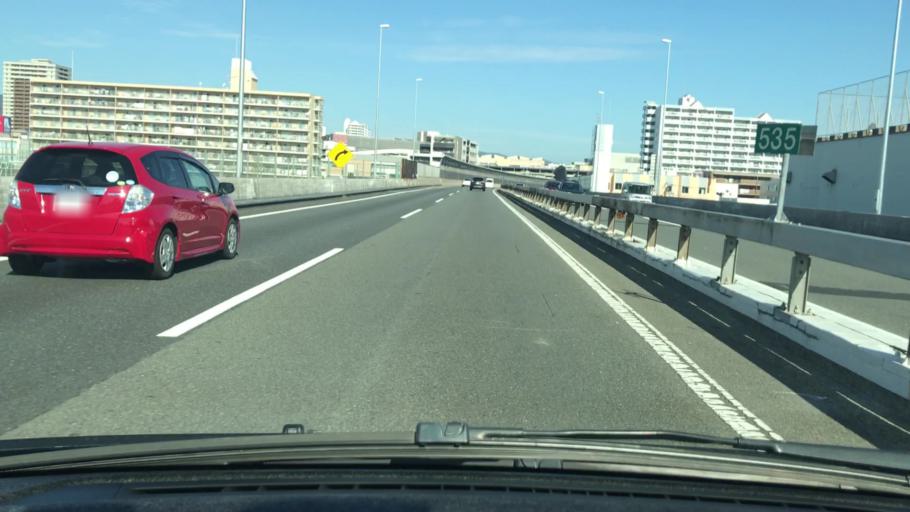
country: JP
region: Hyogo
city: Nishinomiya-hama
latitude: 34.7379
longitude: 135.3595
